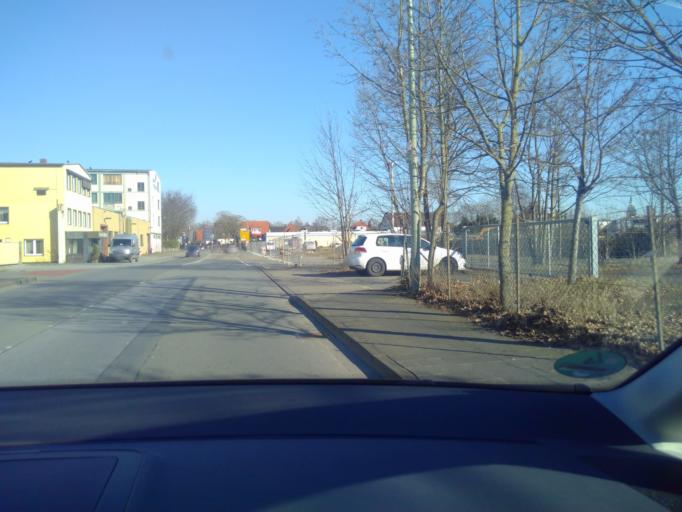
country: DE
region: North Rhine-Westphalia
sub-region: Regierungsbezirk Detmold
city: Rheda-Wiedenbruck
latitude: 51.8363
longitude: 8.3003
